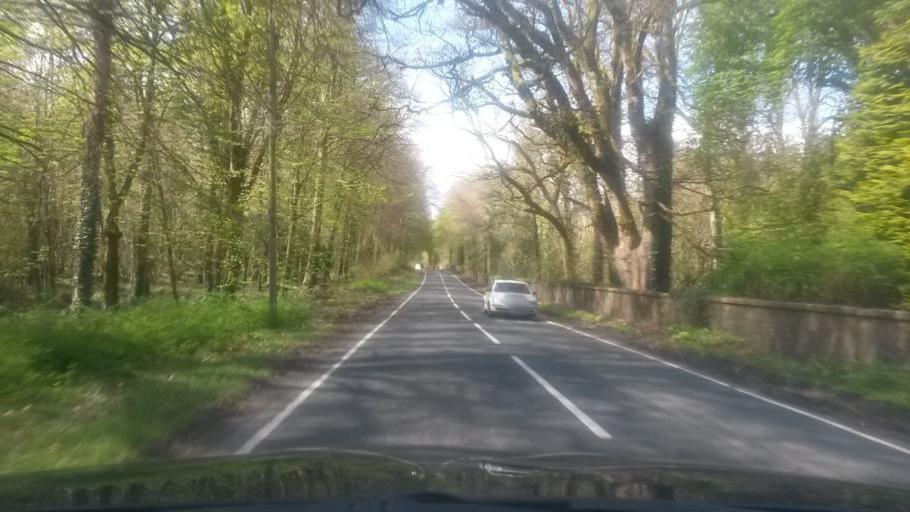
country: GB
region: Northern Ireland
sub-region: Fermanagh District
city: Enniskillen
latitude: 54.3959
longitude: -7.7083
